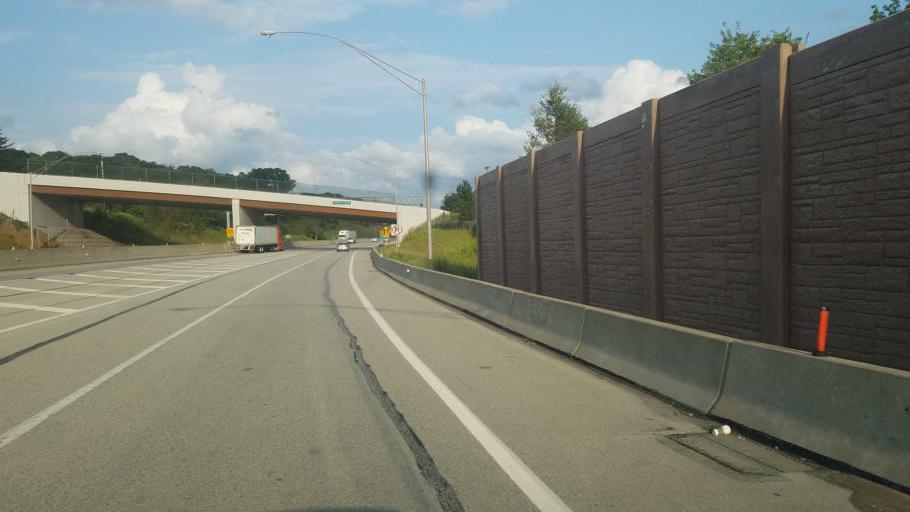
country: US
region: Pennsylvania
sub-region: Allegheny County
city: Bradford Woods
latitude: 40.6548
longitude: -80.0696
